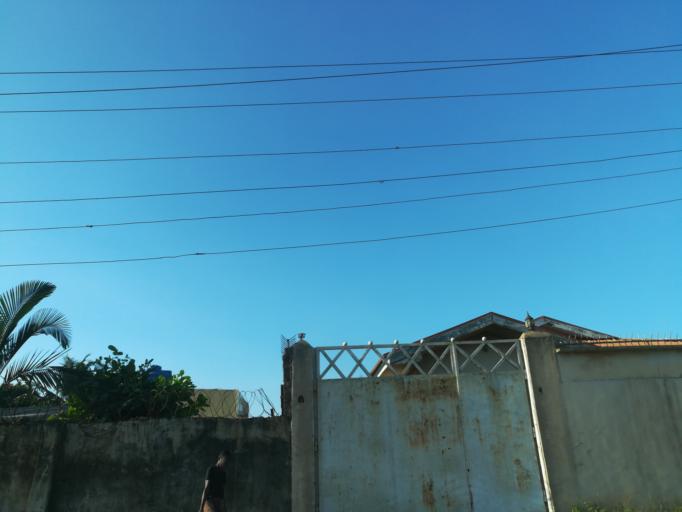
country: NG
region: Lagos
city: Ikorodu
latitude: 6.5820
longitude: 3.5280
